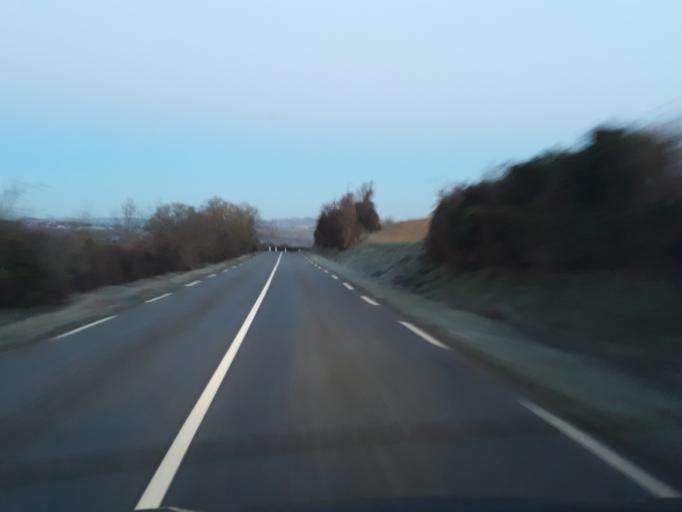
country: FR
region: Midi-Pyrenees
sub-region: Departement du Gers
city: Samatan
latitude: 43.4708
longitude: 0.9665
